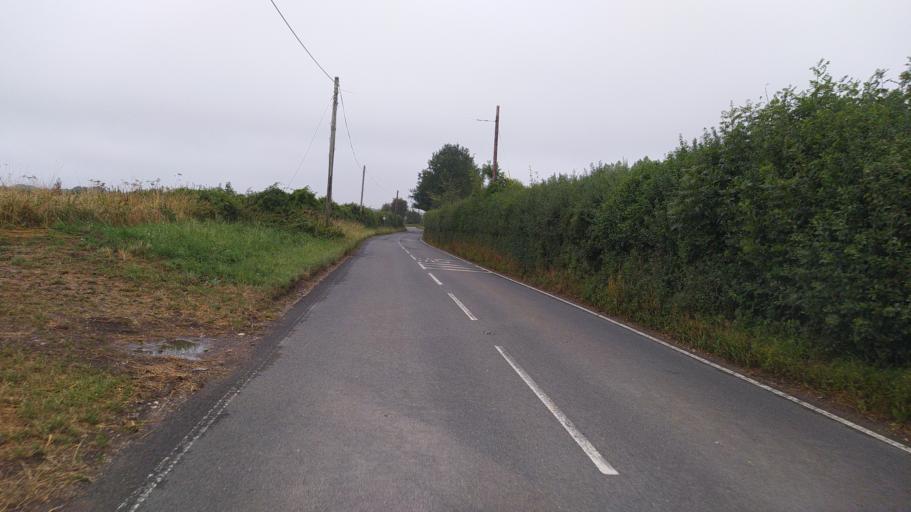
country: GB
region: England
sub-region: Wiltshire
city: Bower Chalke
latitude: 50.9560
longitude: -2.0143
